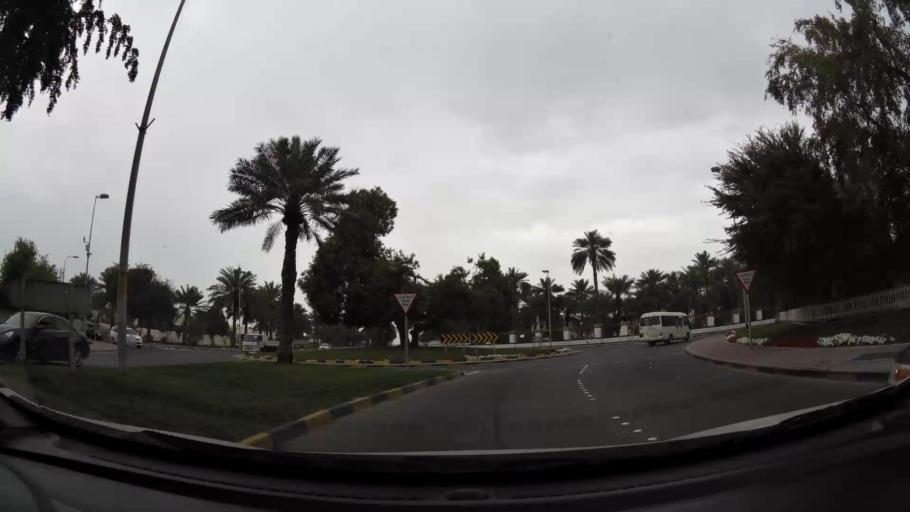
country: BH
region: Northern
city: Ar Rifa'
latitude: 26.1217
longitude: 50.5360
